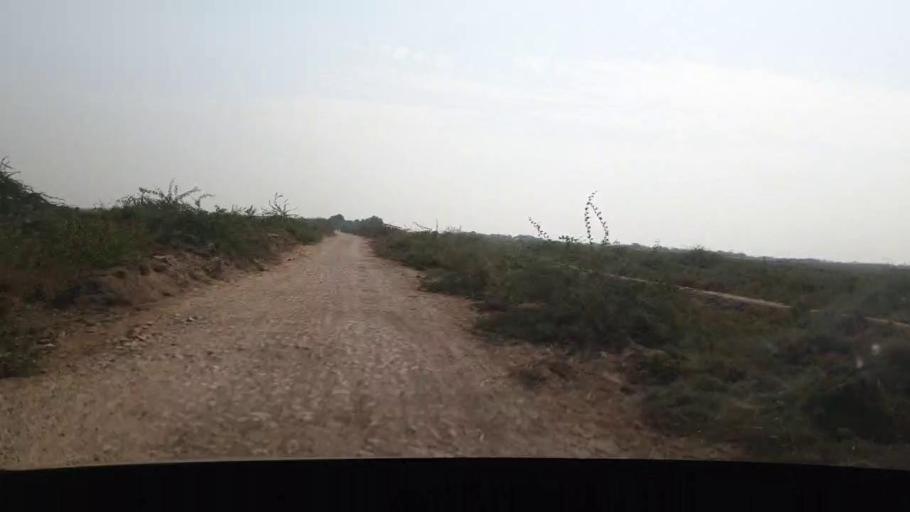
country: PK
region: Sindh
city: Chuhar Jamali
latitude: 24.2473
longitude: 67.9912
